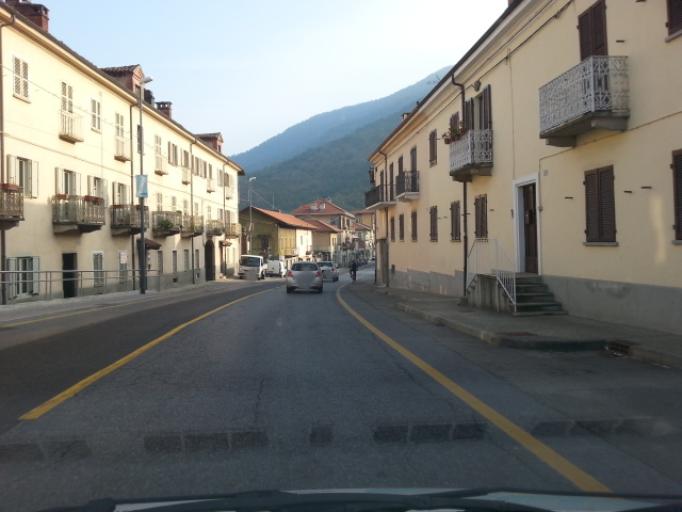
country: IT
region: Piedmont
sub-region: Provincia di Torino
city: Trana
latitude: 45.0383
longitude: 7.4190
